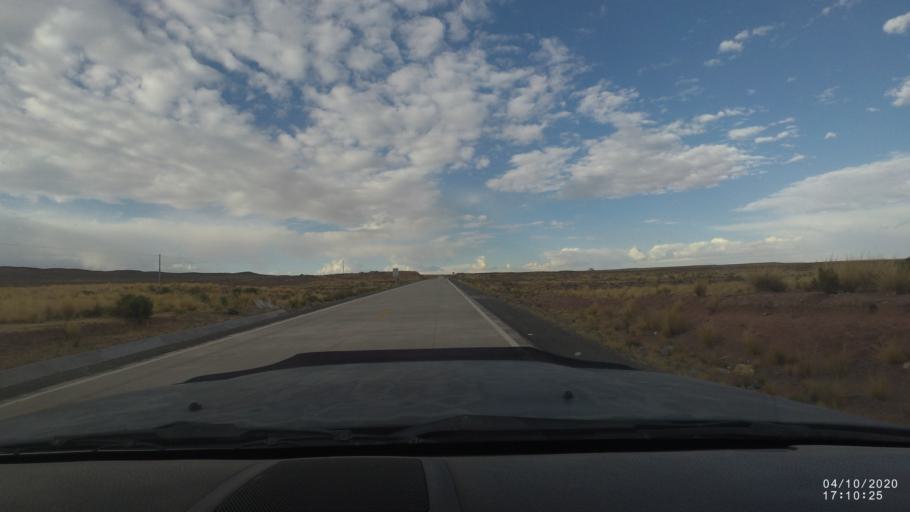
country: BO
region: Oruro
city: Oruro
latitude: -18.3315
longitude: -67.5843
